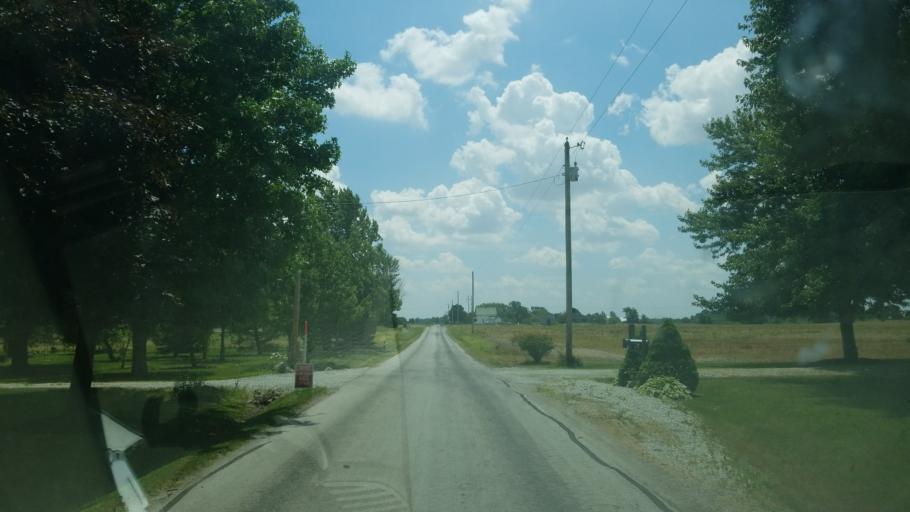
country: US
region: Ohio
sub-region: Hardin County
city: Kenton
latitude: 40.6200
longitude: -83.5596
